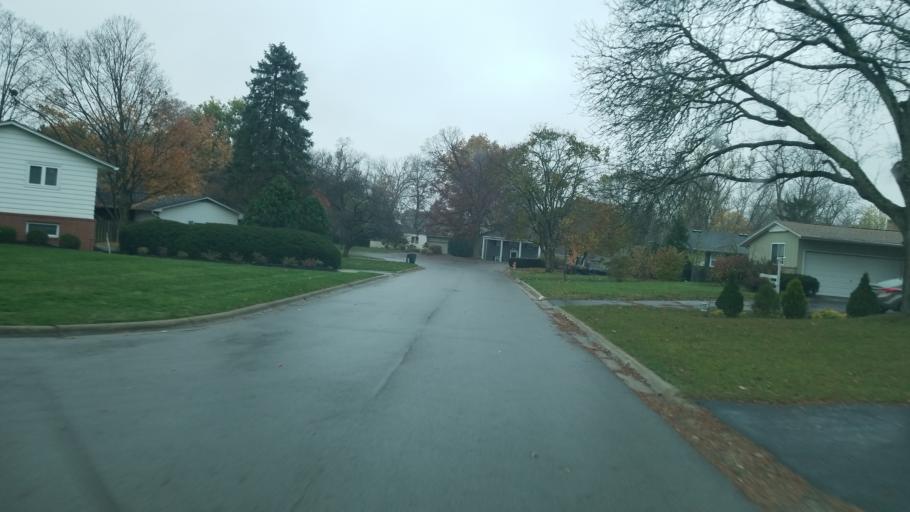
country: US
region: Ohio
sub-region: Franklin County
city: Upper Arlington
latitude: 40.0363
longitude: -83.0456
